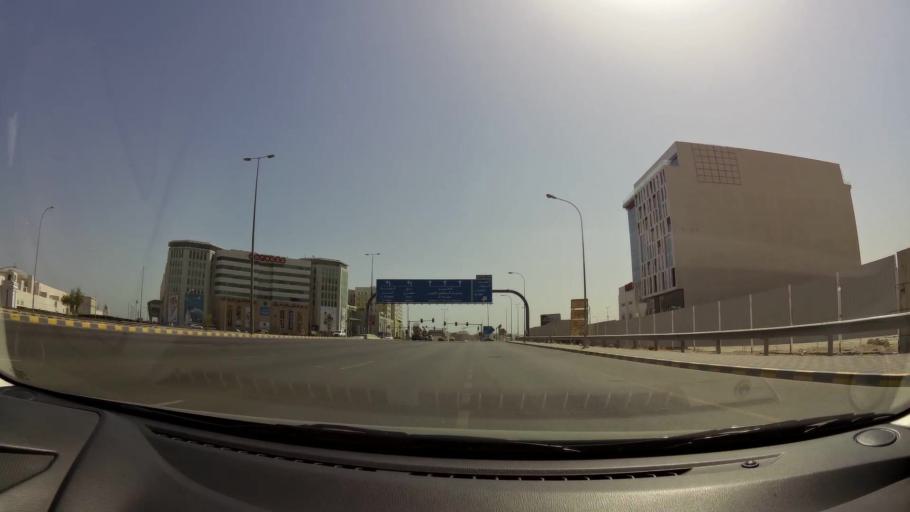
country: OM
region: Muhafazat Masqat
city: Bawshar
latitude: 23.5865
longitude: 58.4119
